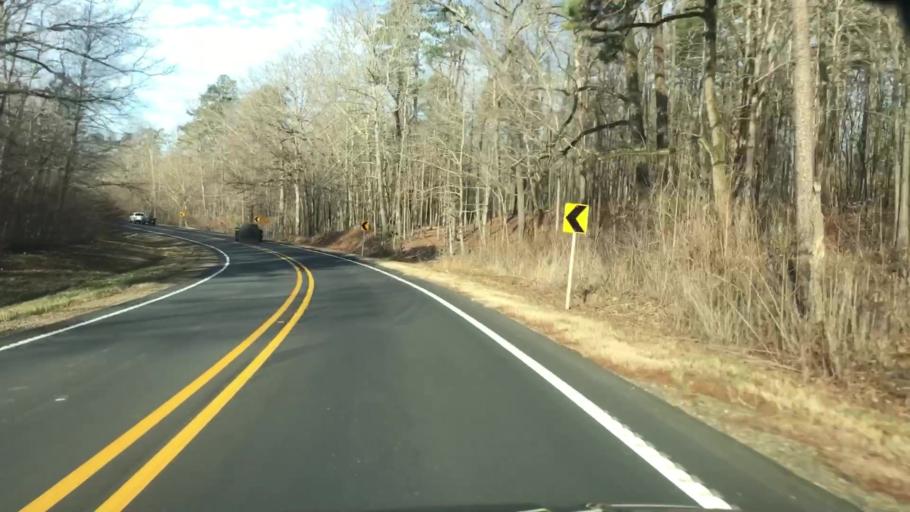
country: US
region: Arkansas
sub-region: Montgomery County
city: Mount Ida
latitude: 34.5233
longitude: -93.3926
